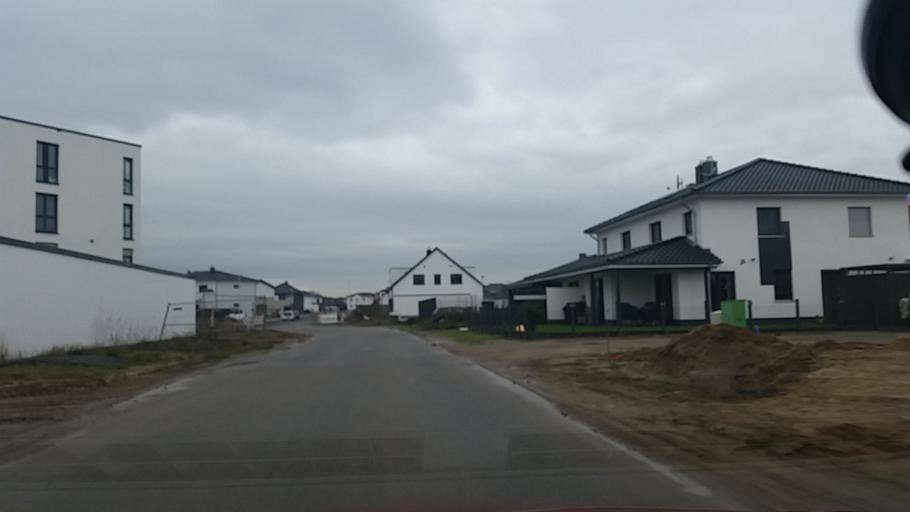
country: DE
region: Lower Saxony
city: Ruhen
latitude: 52.4619
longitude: 10.8426
